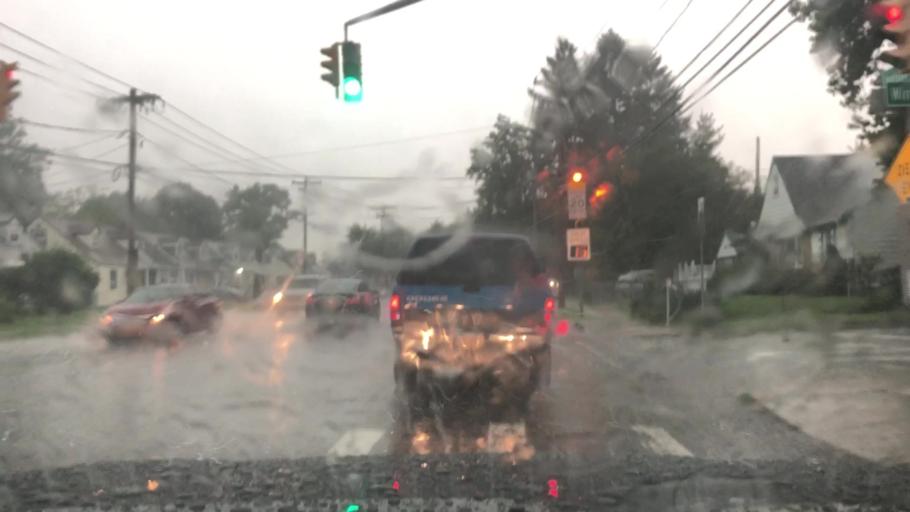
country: US
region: New York
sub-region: Nassau County
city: Uniondale
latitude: 40.6947
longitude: -73.5807
